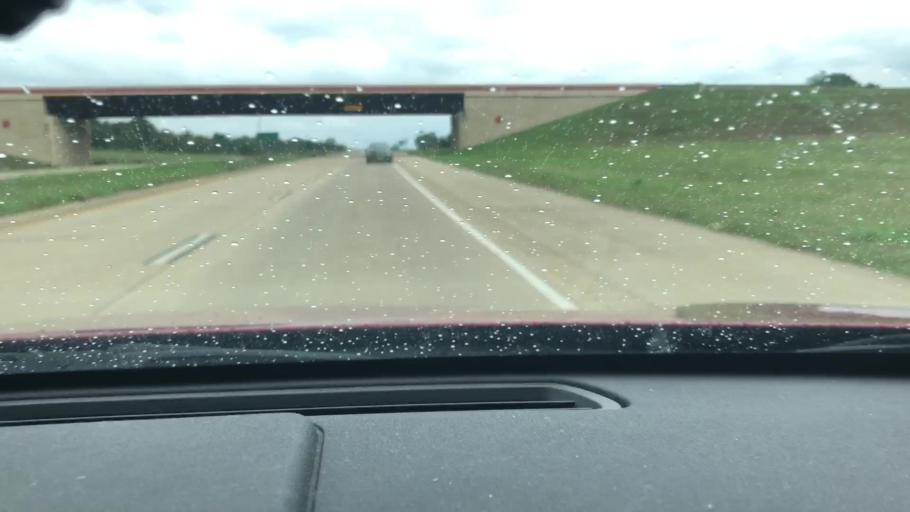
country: US
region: Texas
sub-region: Bowie County
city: Texarkana
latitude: 33.3857
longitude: -94.0441
